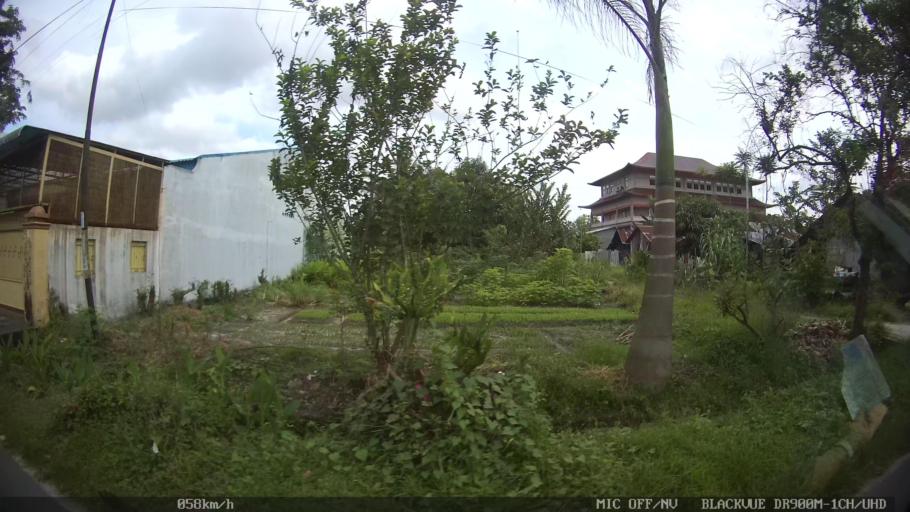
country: ID
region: North Sumatra
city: Percut
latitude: 3.5619
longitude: 98.8691
